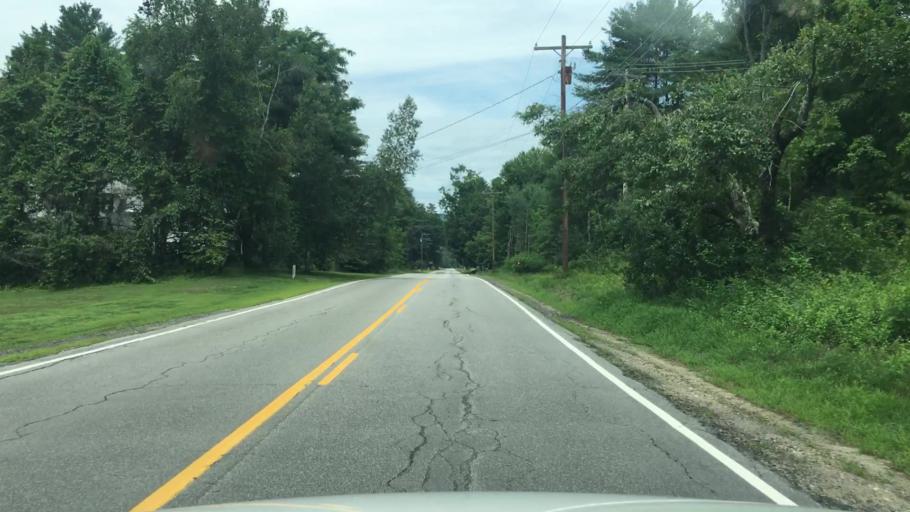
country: US
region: New Hampshire
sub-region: Grafton County
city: Rumney
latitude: 43.7869
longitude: -71.7733
